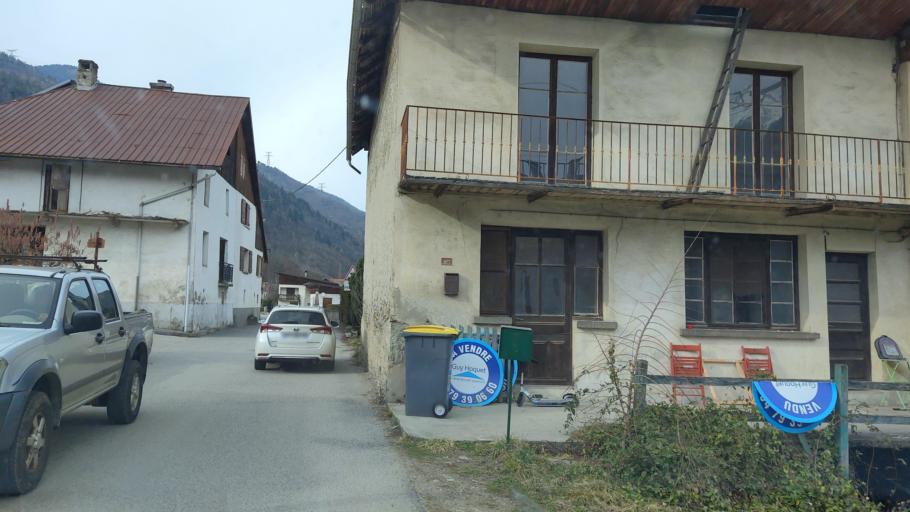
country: FR
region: Rhone-Alpes
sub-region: Departement de la Savoie
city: La Bathie
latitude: 45.6113
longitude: 6.4370
